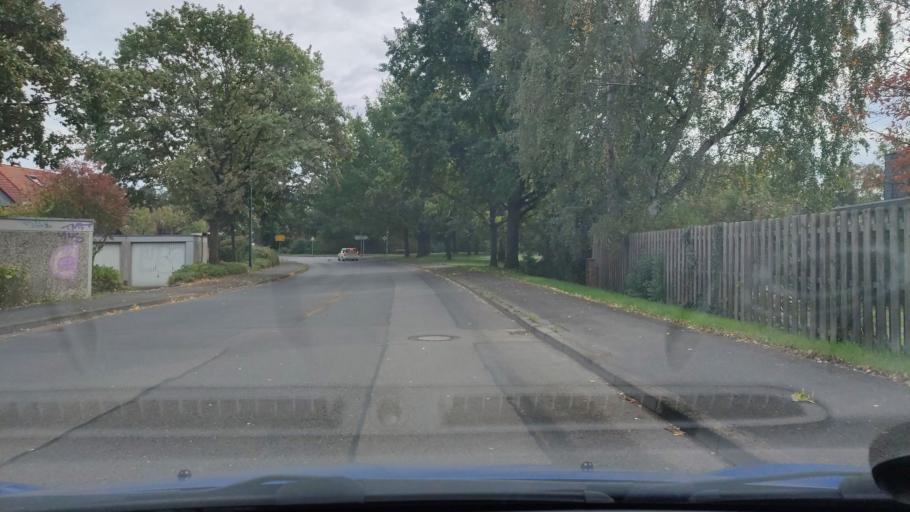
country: DE
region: Lower Saxony
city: Langenhagen
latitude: 52.4327
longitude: 9.7083
